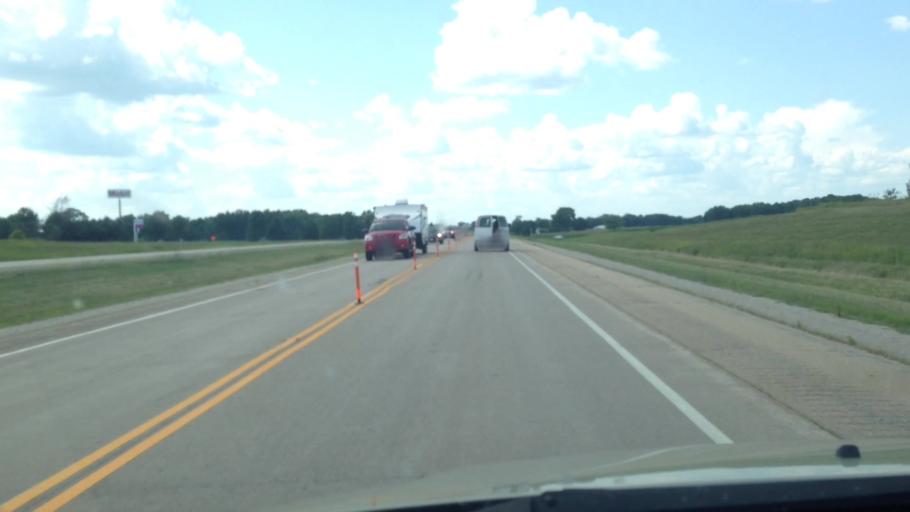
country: US
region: Wisconsin
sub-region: Brown County
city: Pulaski
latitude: 44.6920
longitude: -88.3337
